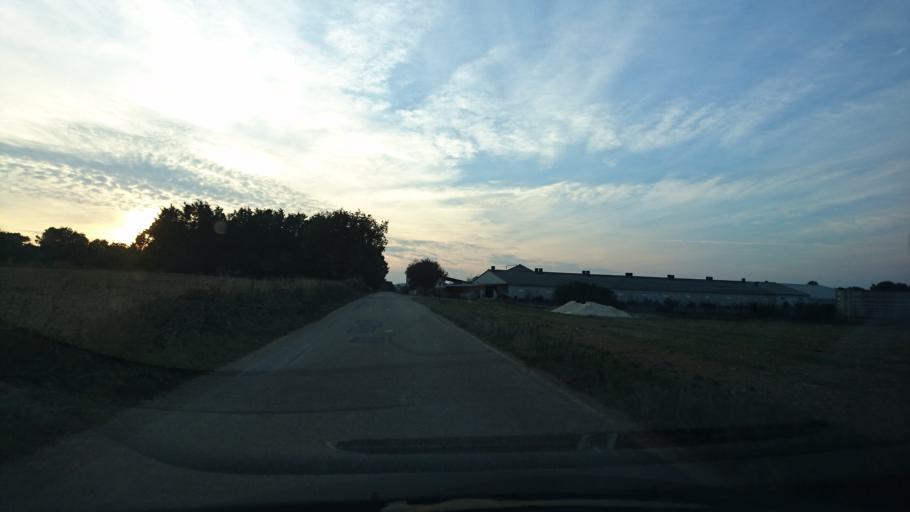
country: FR
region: Brittany
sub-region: Departement du Morbihan
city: Guer
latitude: 47.8670
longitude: -2.0635
